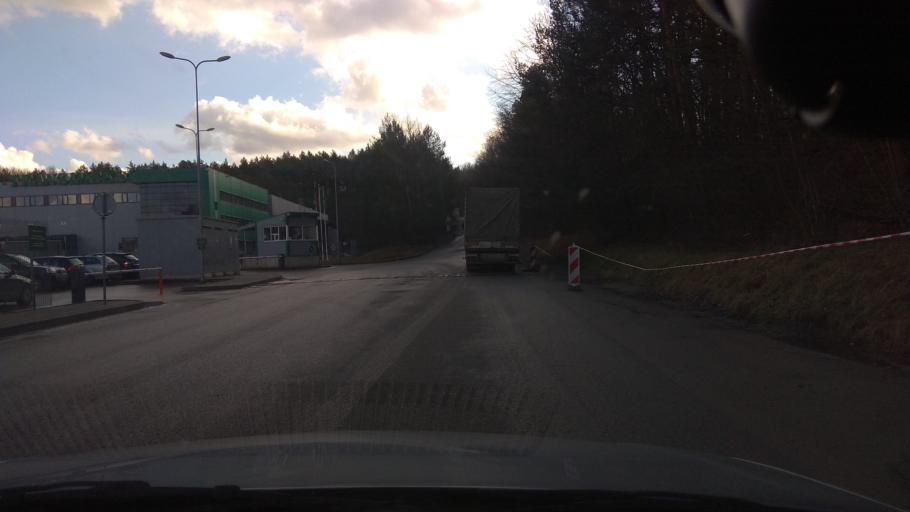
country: LT
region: Vilnius County
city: Lazdynai
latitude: 54.6439
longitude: 25.2221
